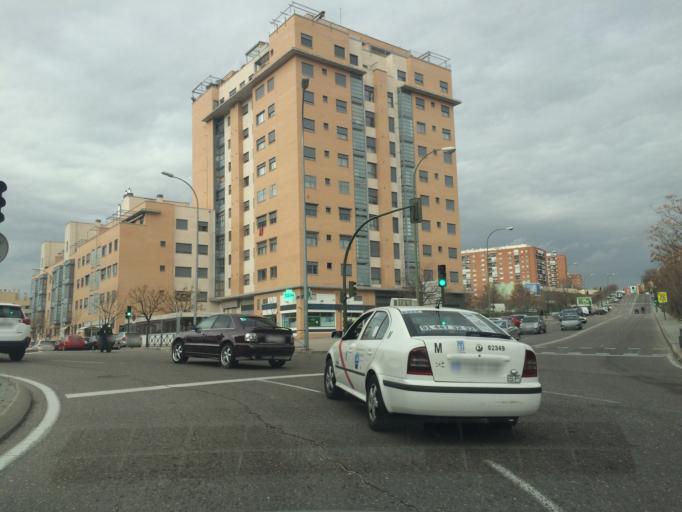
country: ES
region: Madrid
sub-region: Provincia de Madrid
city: Tetuan de las Victorias
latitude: 40.4697
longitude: -3.7143
